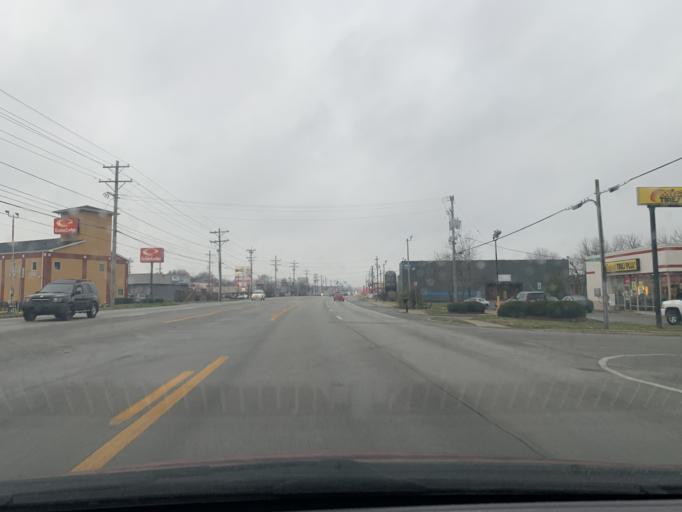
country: US
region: Kentucky
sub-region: Jefferson County
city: Okolona
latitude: 38.1628
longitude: -85.7005
